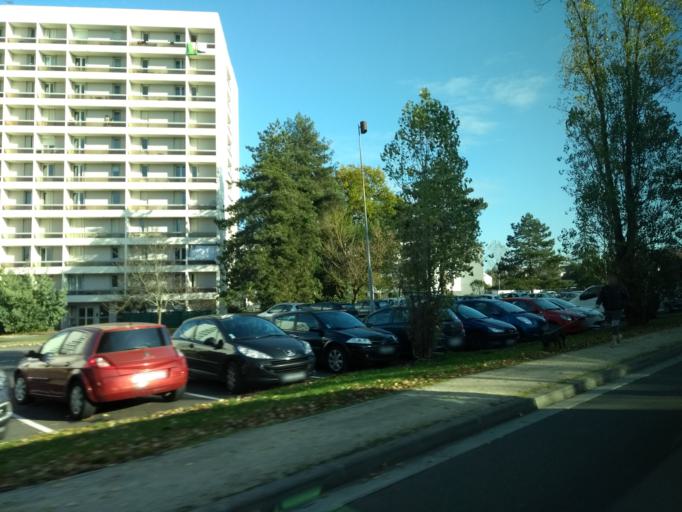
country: FR
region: Aquitaine
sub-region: Departement de la Gironde
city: Gradignan
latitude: 44.7885
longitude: -0.6119
